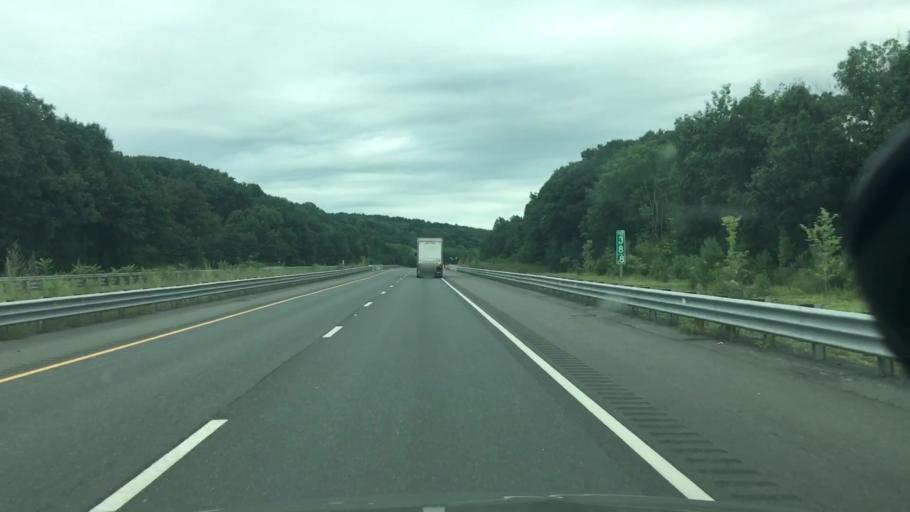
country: US
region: Massachusetts
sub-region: Franklin County
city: South Deerfield
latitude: 42.5250
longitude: -72.6261
